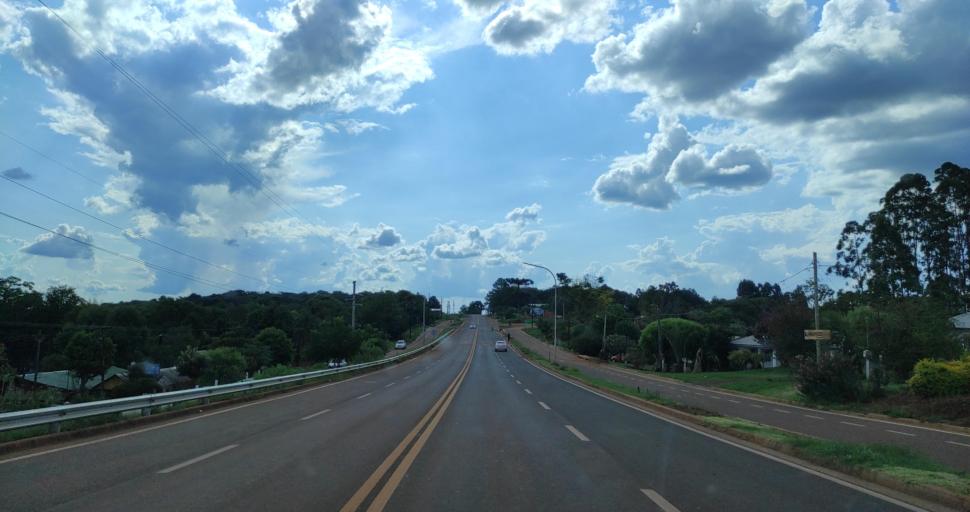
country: AR
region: Misiones
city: Bernardo de Irigoyen
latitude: -26.2936
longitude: -53.7622
